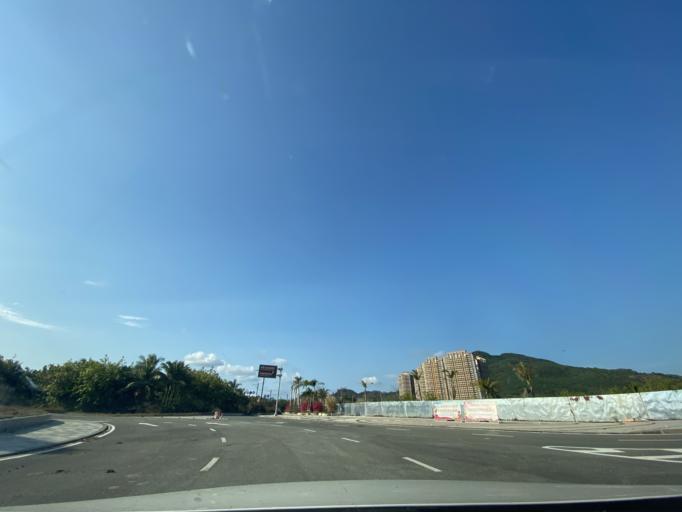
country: CN
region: Hainan
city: Yingzhou
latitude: 18.4530
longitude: 109.8555
